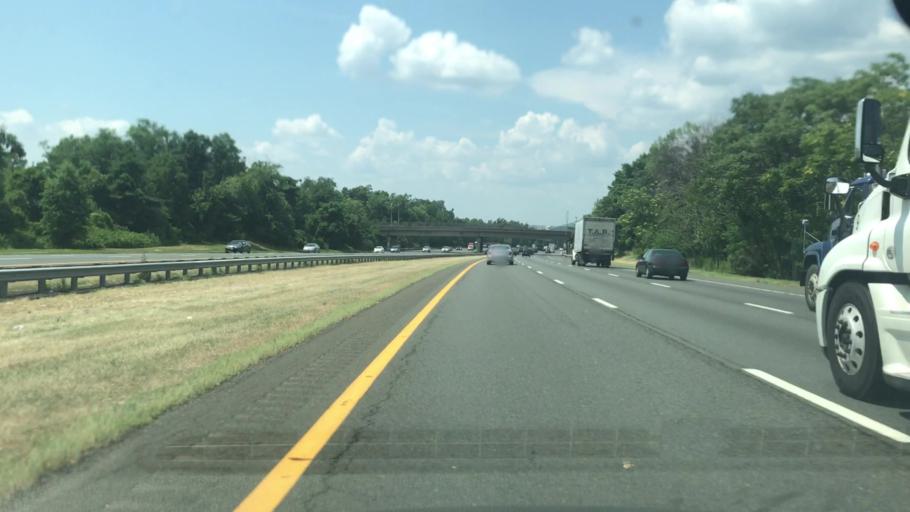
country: US
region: New Jersey
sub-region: Somerset County
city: South Bound Brook
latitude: 40.5458
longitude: -74.5358
